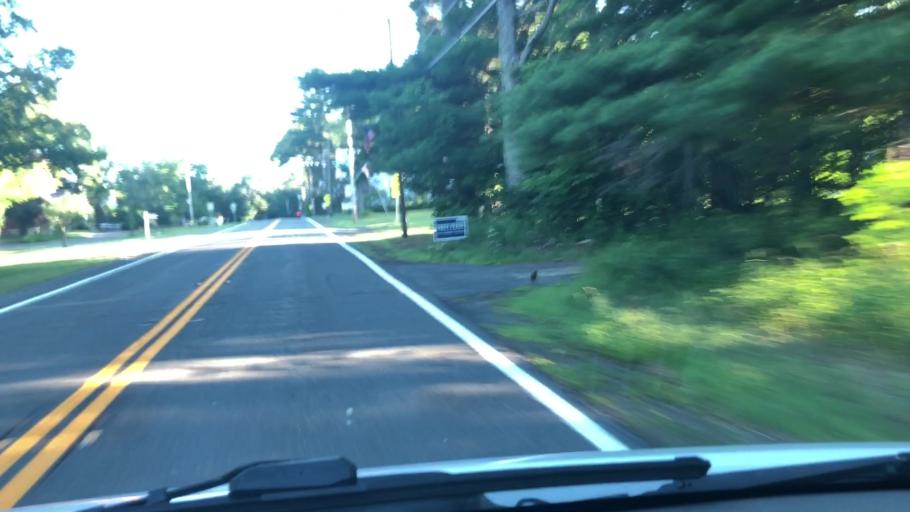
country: US
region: Massachusetts
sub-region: Hampshire County
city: Chesterfield
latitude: 42.3984
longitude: -72.9367
